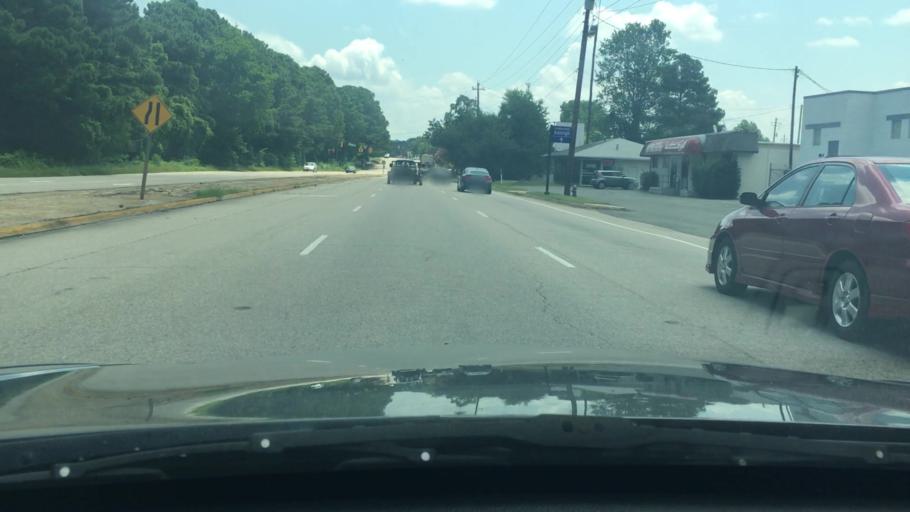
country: US
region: North Carolina
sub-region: Wake County
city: West Raleigh
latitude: 35.7952
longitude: -78.6932
